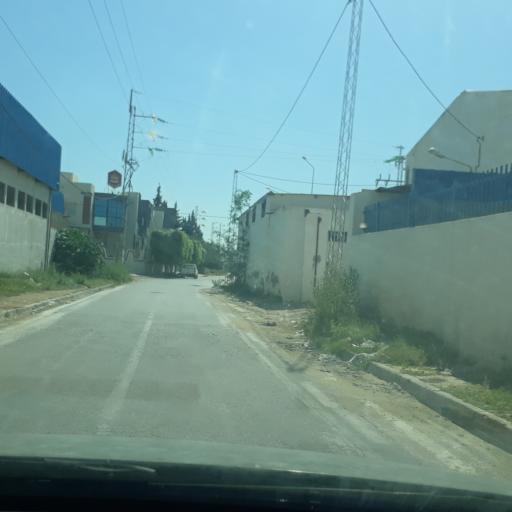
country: TN
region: Safaqis
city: Al Qarmadah
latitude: 34.8342
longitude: 10.7632
